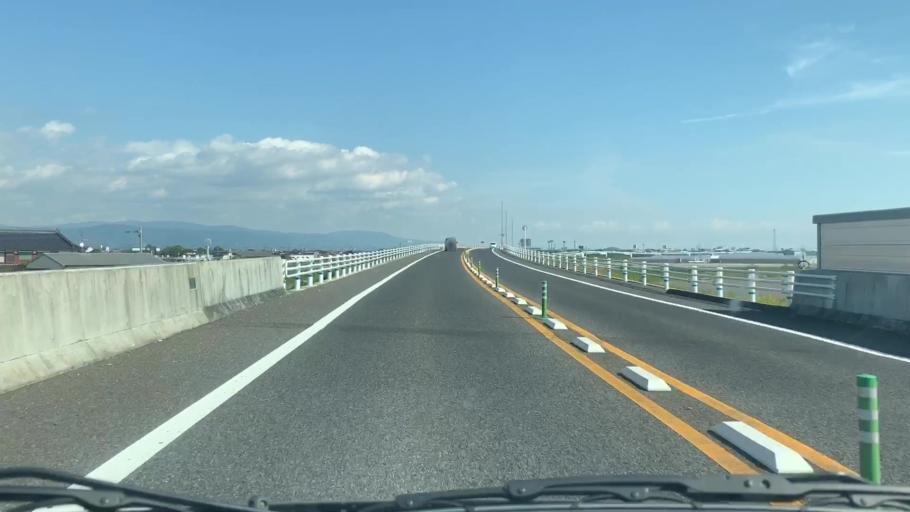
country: JP
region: Saga Prefecture
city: Saga-shi
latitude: 33.2278
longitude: 130.2203
